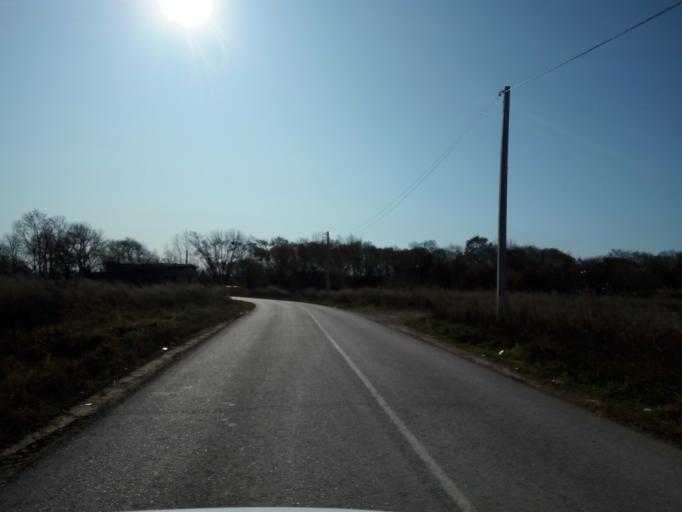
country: RU
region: Primorskiy
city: Dal'nerechensk
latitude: 45.9424
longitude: 133.6871
